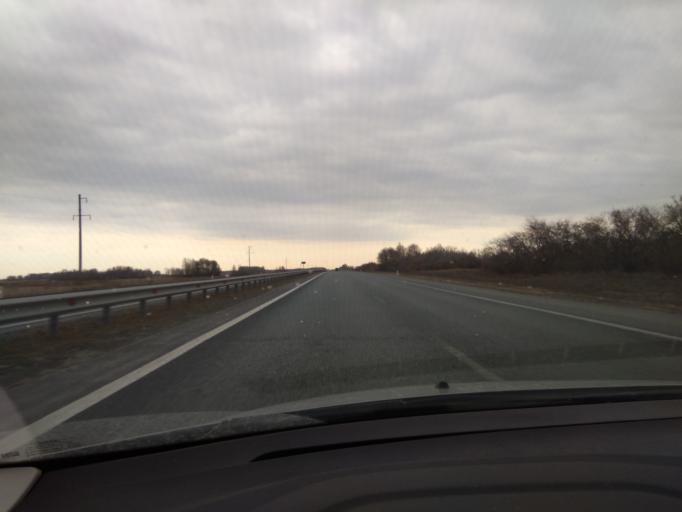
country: RU
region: Chelyabinsk
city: Kunashak
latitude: 55.7430
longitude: 61.2279
